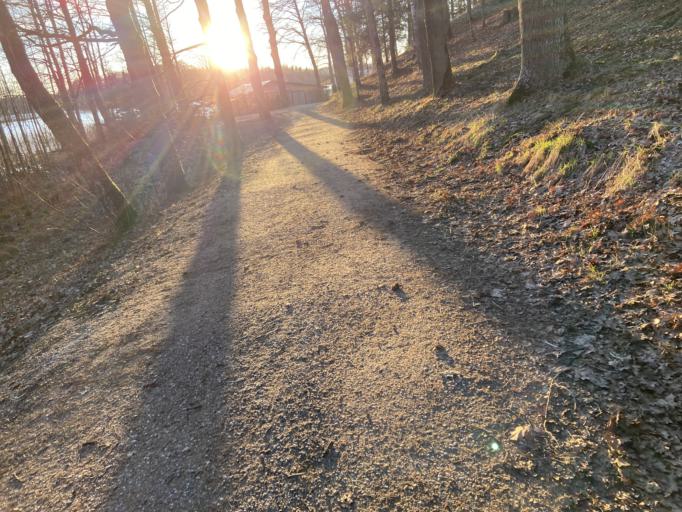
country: EE
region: Vorumaa
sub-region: Antsla vald
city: Vana-Antsla
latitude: 58.0426
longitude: 26.4723
